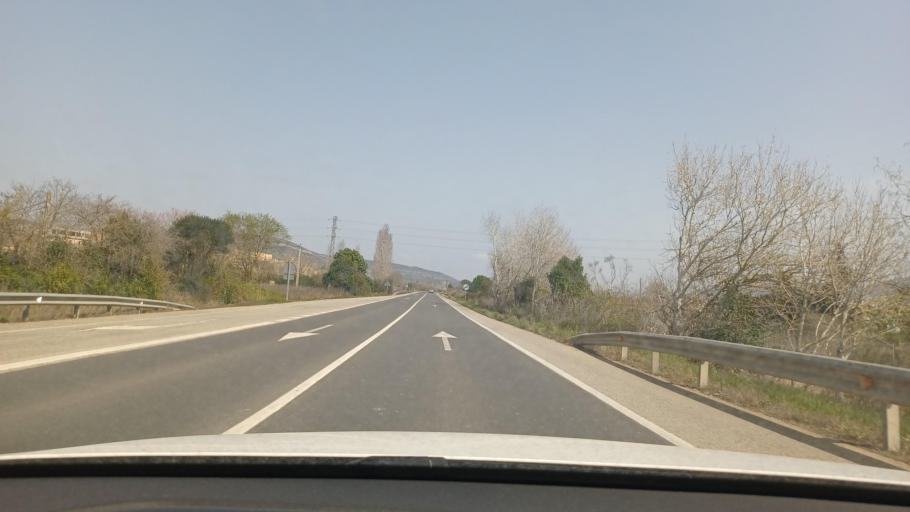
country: ES
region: Catalonia
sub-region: Provincia de Tarragona
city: Ulldecona
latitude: 40.5927
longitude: 0.4489
